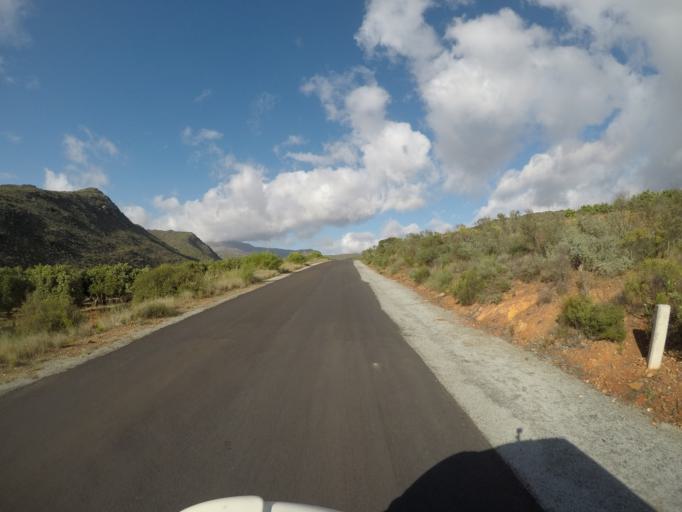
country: ZA
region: Western Cape
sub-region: West Coast District Municipality
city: Clanwilliam
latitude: -32.4329
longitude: 18.9481
